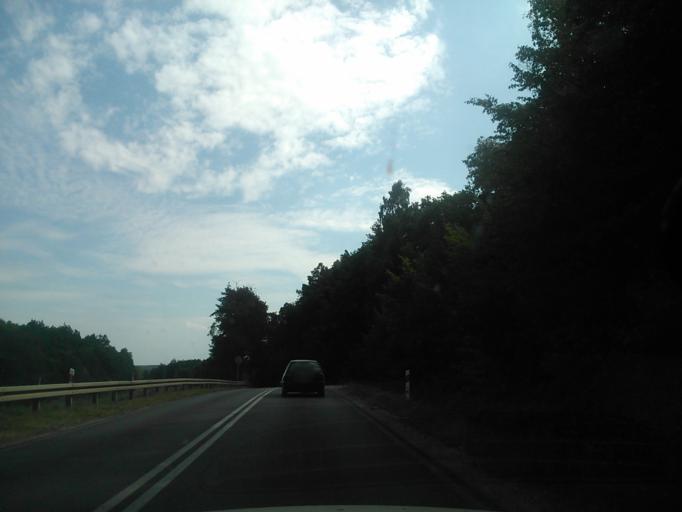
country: PL
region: Warmian-Masurian Voivodeship
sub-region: Powiat dzialdowski
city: Ilowo -Osada
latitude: 53.1576
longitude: 20.3119
